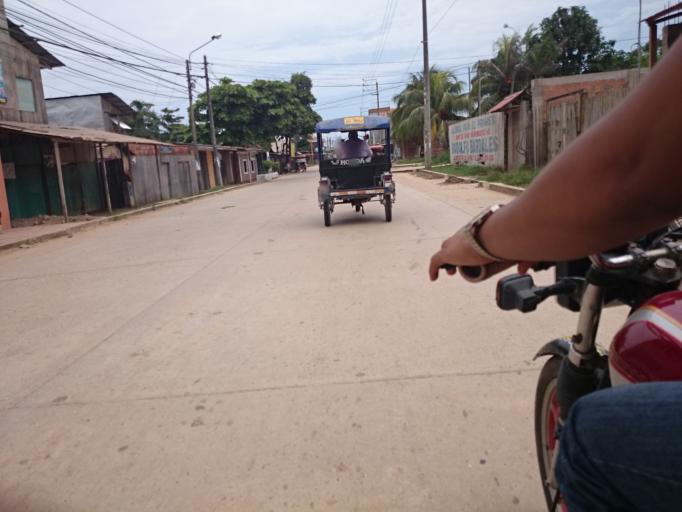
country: PE
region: Ucayali
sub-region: Provincia de Coronel Portillo
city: Pucallpa
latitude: -8.3742
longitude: -74.5588
